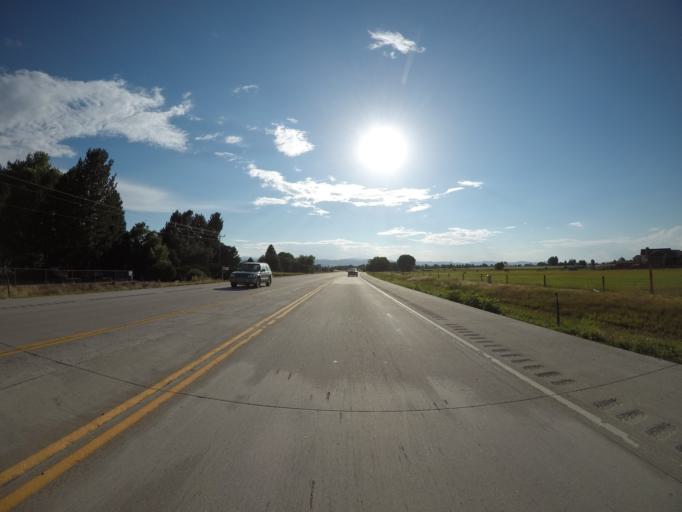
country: US
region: Colorado
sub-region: Larimer County
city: Fort Collins
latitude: 40.5810
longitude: -104.9674
